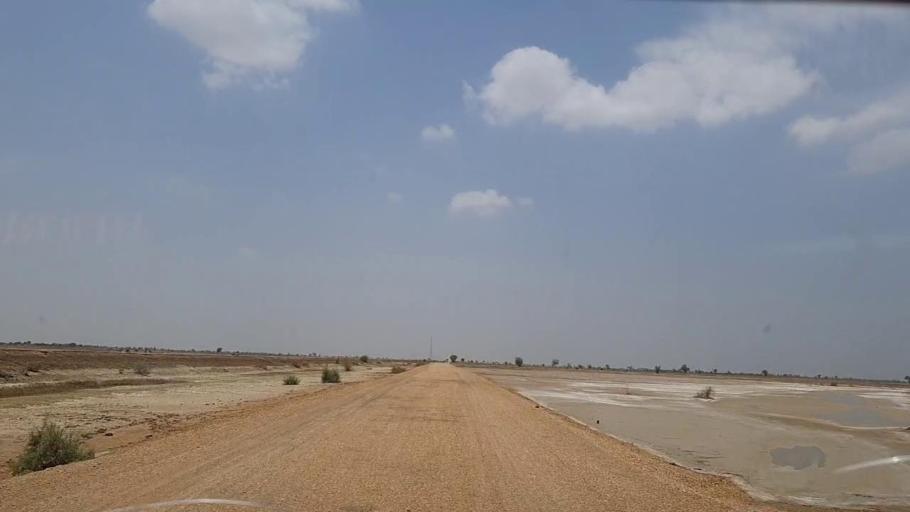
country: PK
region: Sindh
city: Johi
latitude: 26.7715
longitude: 67.6566
